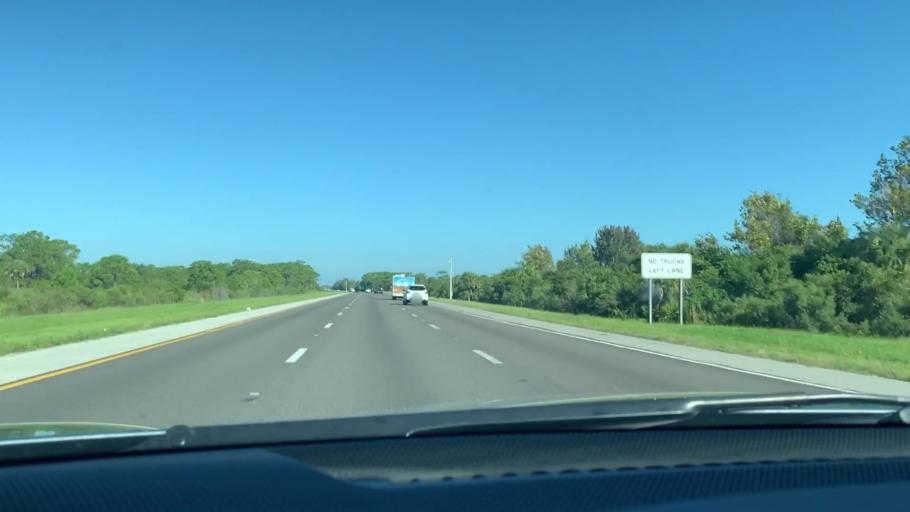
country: US
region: Florida
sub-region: Sarasota County
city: Nokomis
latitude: 27.1431
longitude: -82.4117
